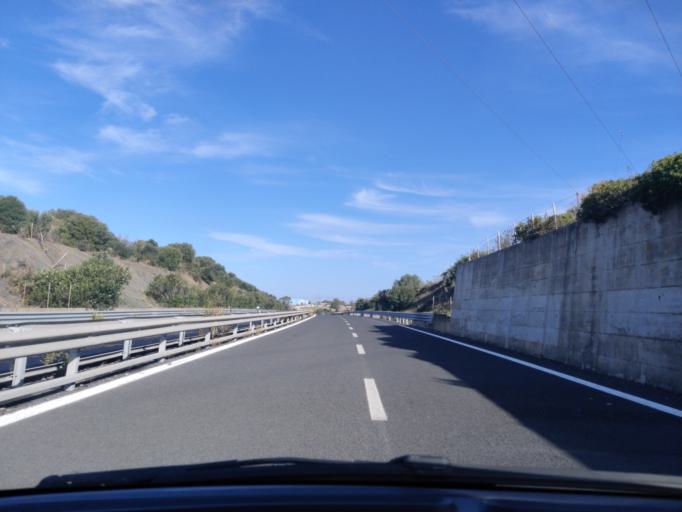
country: IT
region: Latium
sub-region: Citta metropolitana di Roma Capitale
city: Civitavecchia
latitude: 42.1147
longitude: 11.7927
